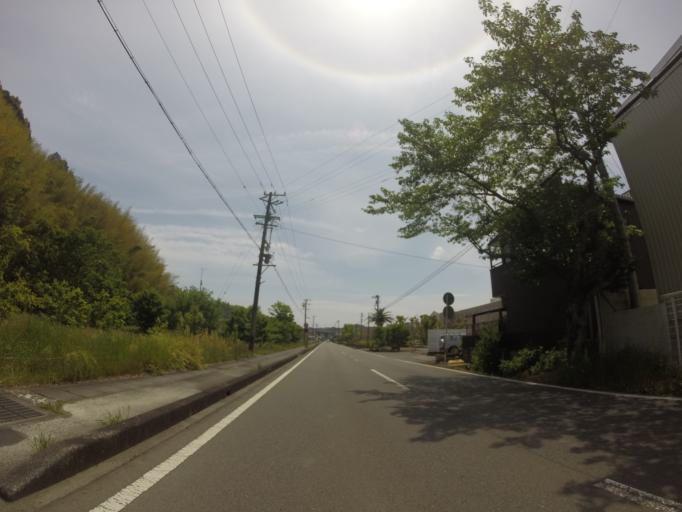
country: JP
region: Shizuoka
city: Fujieda
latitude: 34.9102
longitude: 138.2467
